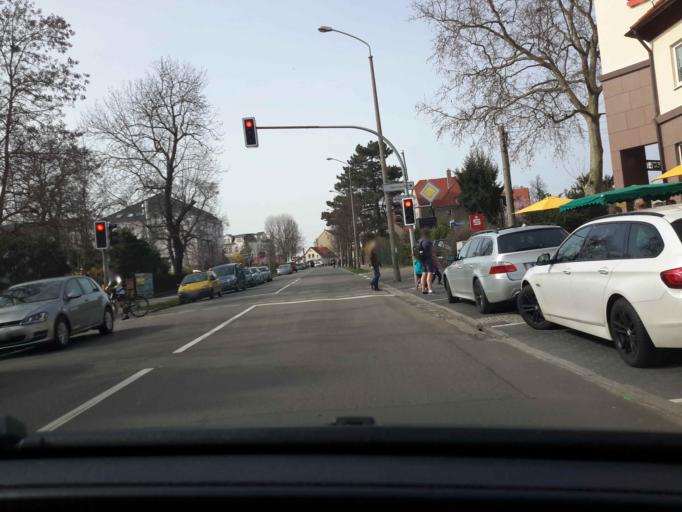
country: DE
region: Saxony
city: Rackwitz
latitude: 51.3947
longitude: 12.3728
